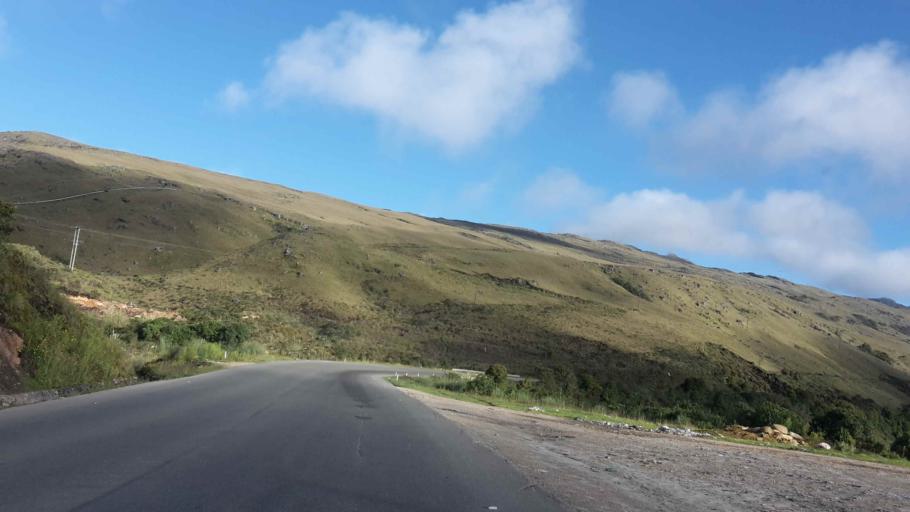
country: BO
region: Cochabamba
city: Colomi
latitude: -17.2268
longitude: -65.8890
